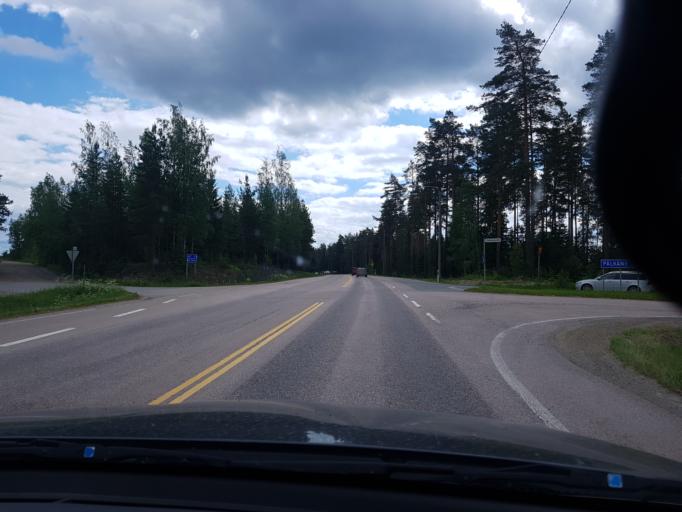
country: FI
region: Pirkanmaa
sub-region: Tampere
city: Paelkaene
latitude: 61.3171
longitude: 24.2847
